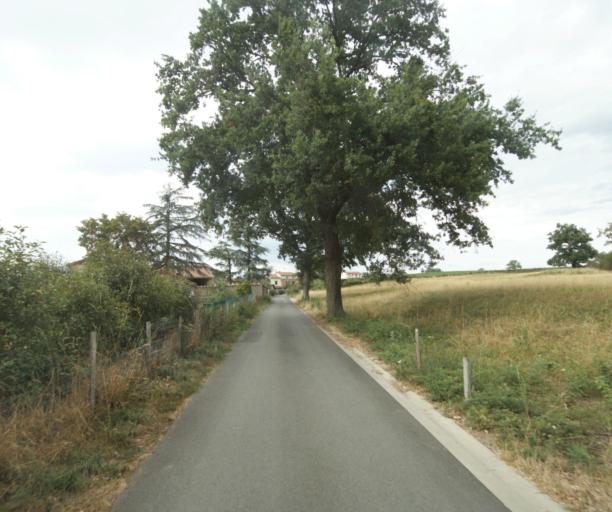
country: FR
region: Rhone-Alpes
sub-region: Departement du Rhone
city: Saint-Romain-de-Popey
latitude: 45.8814
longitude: 4.5414
